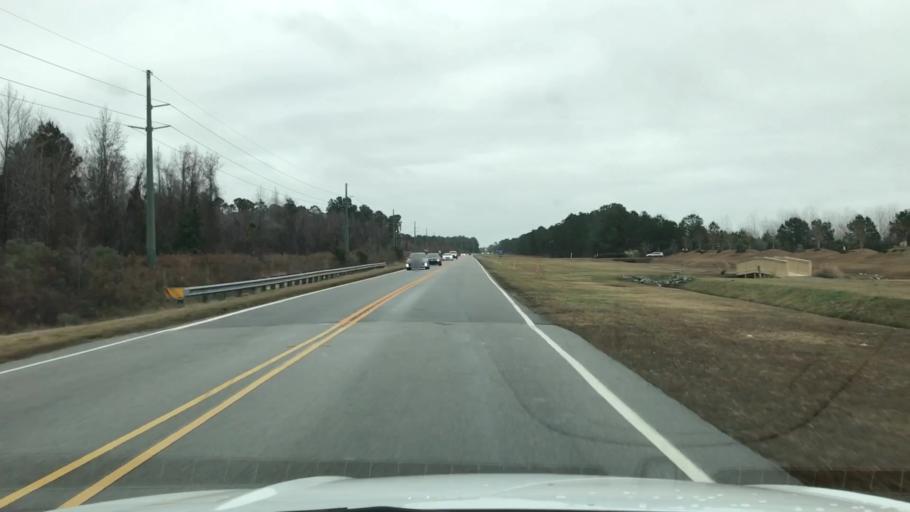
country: US
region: South Carolina
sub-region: Horry County
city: Myrtle Beach
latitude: 33.7379
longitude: -78.8944
